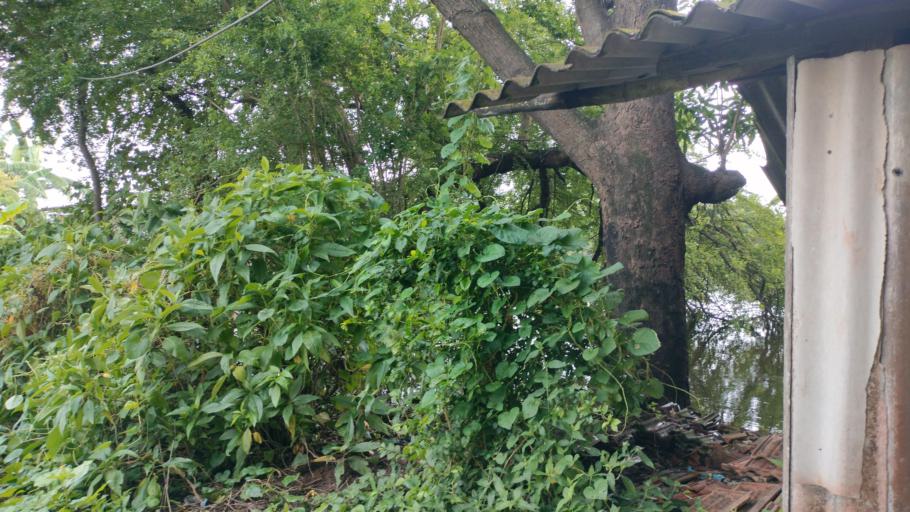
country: IN
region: Maharashtra
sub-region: Thane
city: Virar
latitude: 19.4082
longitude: 72.8054
